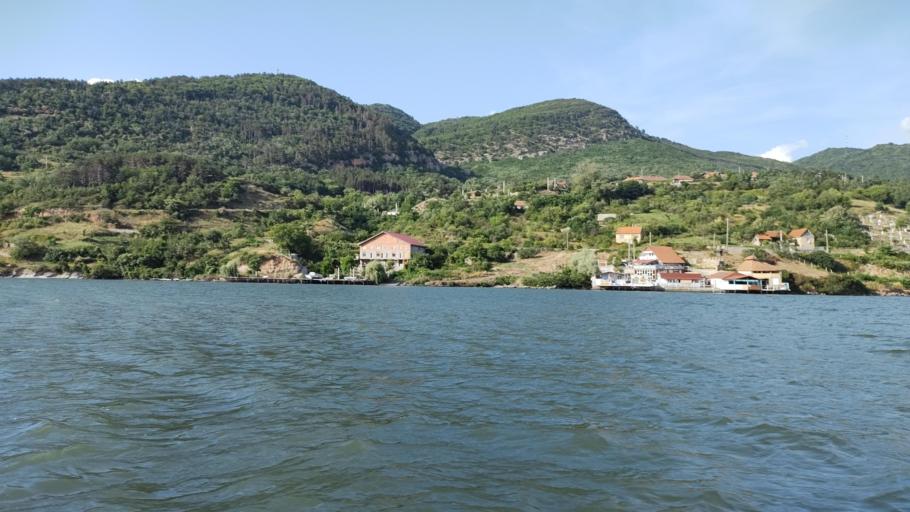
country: RO
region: Mehedinti
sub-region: Comuna Svinita
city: Svinita
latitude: 44.4974
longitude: 22.0936
